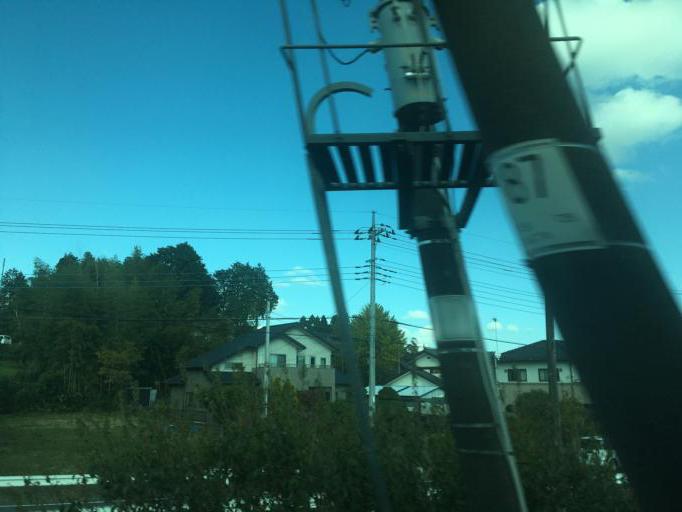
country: JP
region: Ibaraki
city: Tomobe
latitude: 36.3470
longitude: 140.2848
